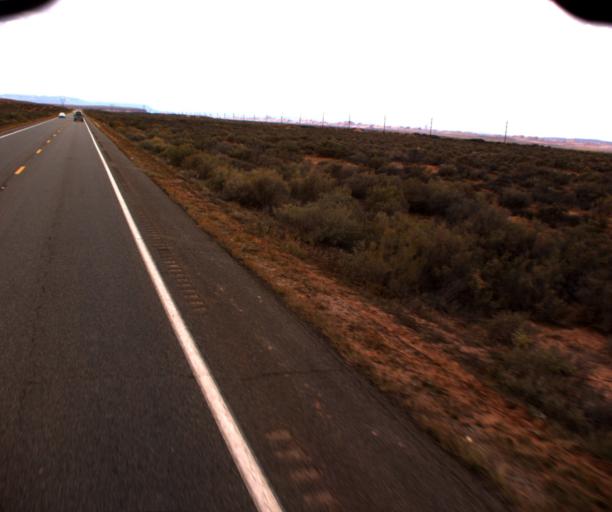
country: US
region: Arizona
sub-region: Navajo County
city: Kayenta
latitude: 36.8084
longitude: -109.9062
